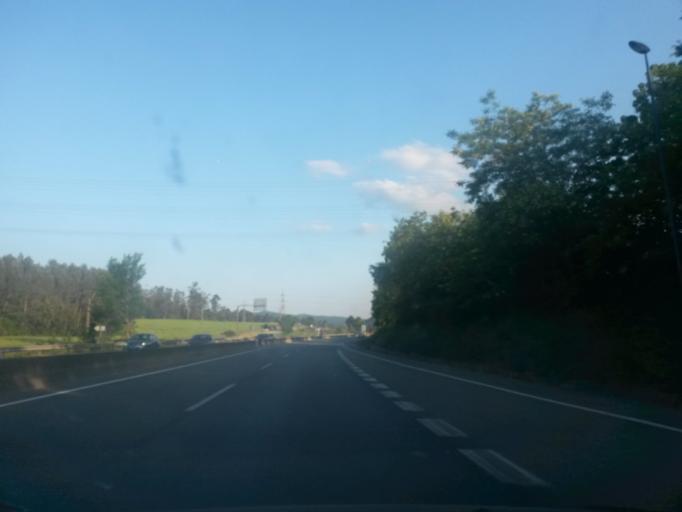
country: ES
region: Catalonia
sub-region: Provincia de Girona
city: Palol de Revardit
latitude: 42.0554
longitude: 2.8166
